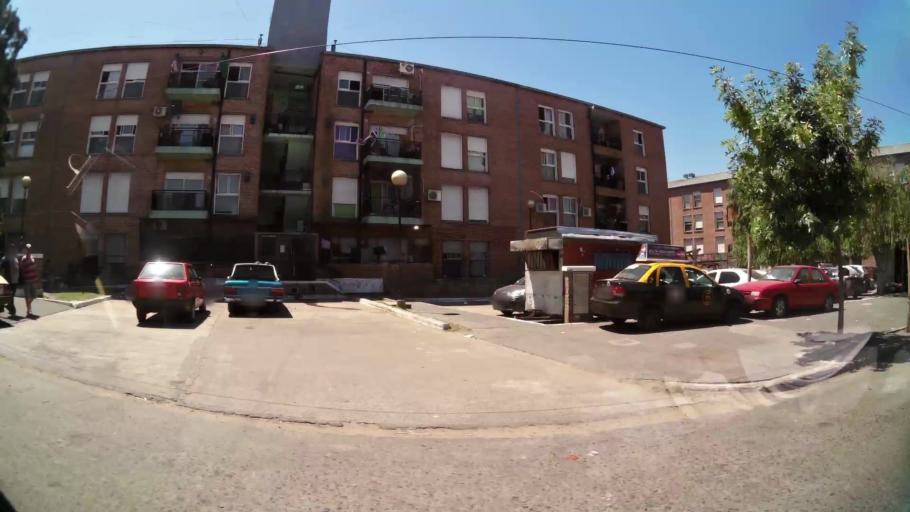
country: AR
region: Buenos Aires
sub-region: Partido de Avellaneda
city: Avellaneda
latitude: -34.6508
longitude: -58.4022
